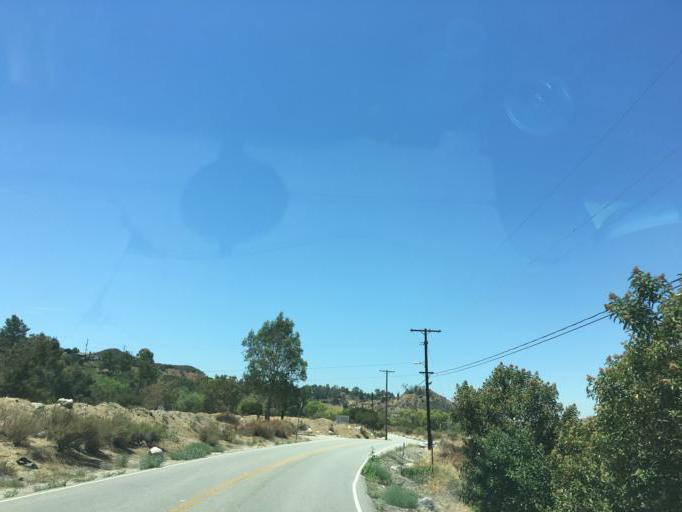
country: US
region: California
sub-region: Los Angeles County
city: La Crescenta-Montrose
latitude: 34.2822
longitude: -118.2938
